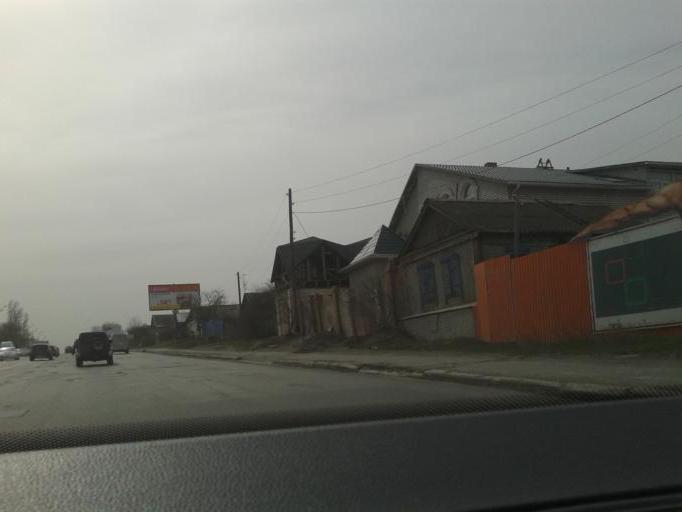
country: RU
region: Volgograd
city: Volgograd
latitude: 48.7024
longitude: 44.4790
